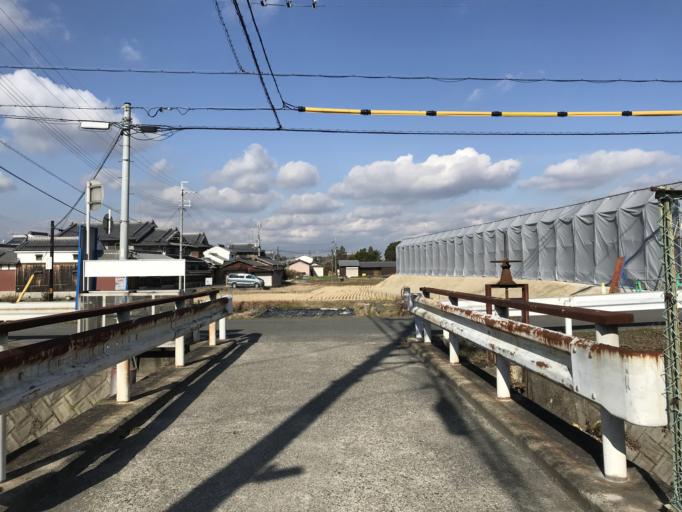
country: JP
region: Nara
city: Nara-shi
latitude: 34.6674
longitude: 135.7870
